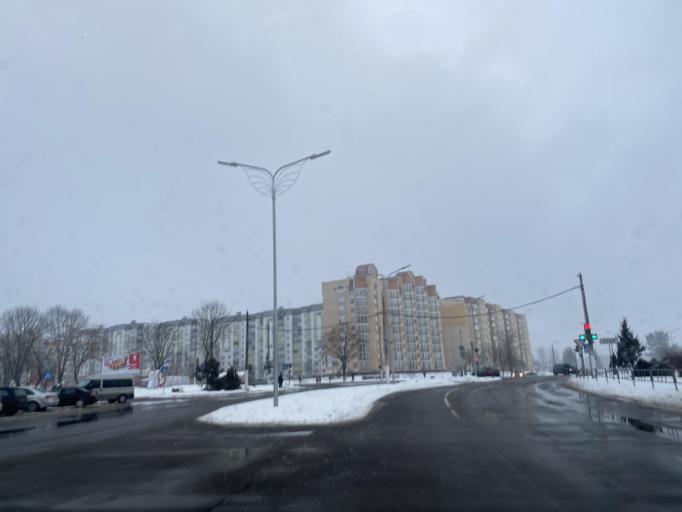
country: BY
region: Minsk
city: Horad Zhodzina
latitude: 54.0971
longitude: 28.3017
